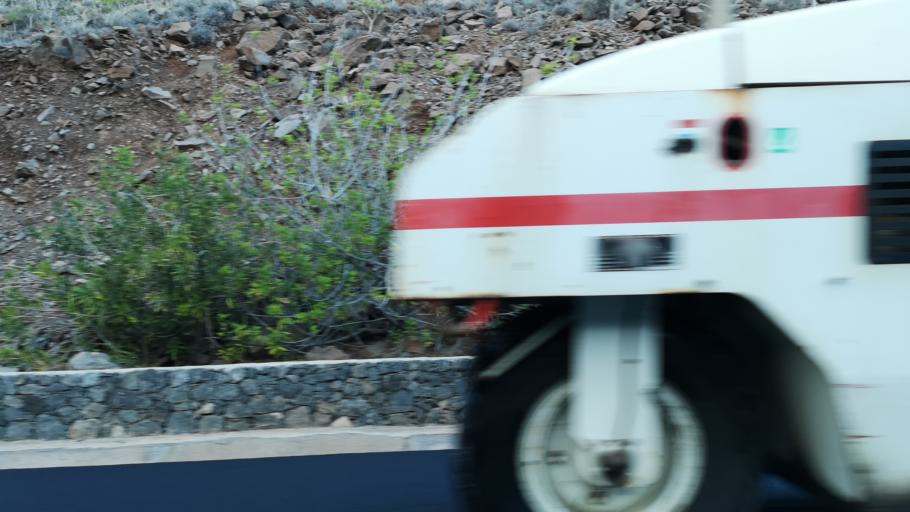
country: ES
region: Canary Islands
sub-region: Provincia de Santa Cruz de Tenerife
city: Alajero
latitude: 28.0343
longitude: -17.2036
